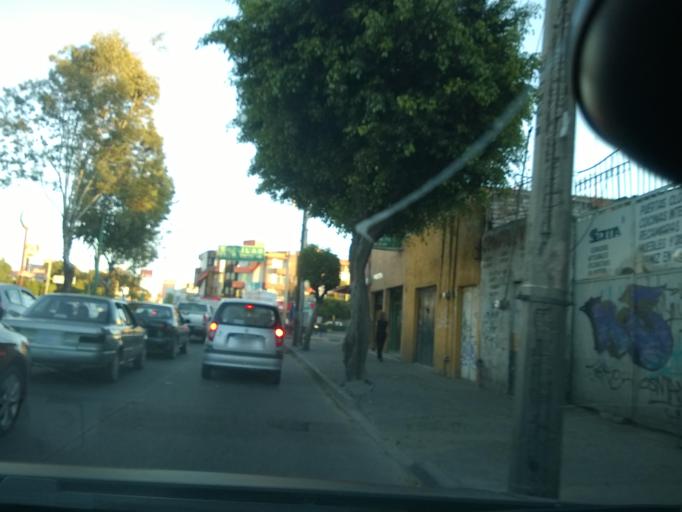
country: MX
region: Guanajuato
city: Leon
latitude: 21.1122
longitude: -101.6766
